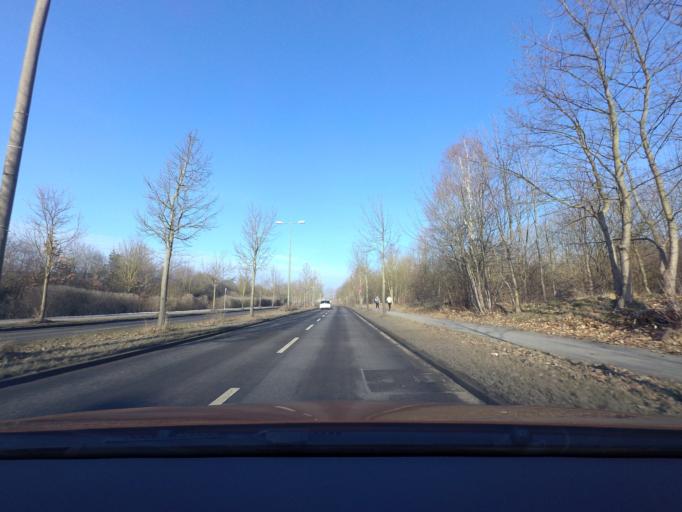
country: DE
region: Berlin
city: Blankenfelde
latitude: 52.6134
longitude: 13.3959
